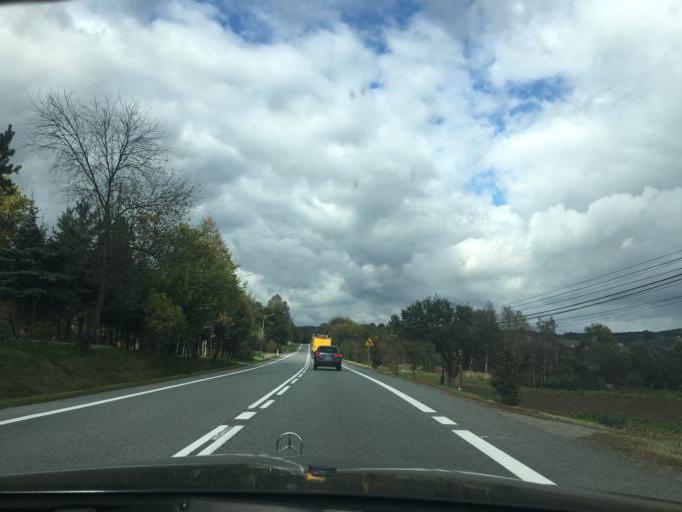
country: PL
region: Subcarpathian Voivodeship
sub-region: Powiat strzyzowski
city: Polomia
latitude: 49.8850
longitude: 21.8999
